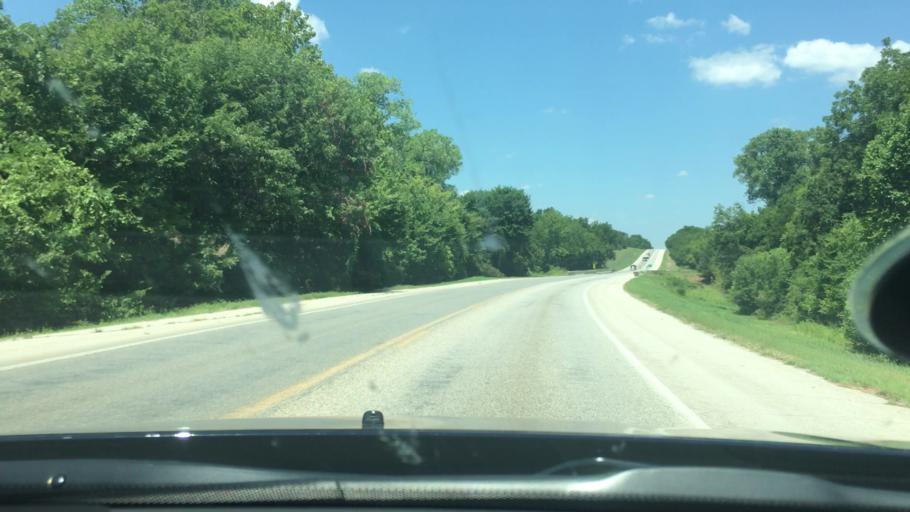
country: US
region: Oklahoma
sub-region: Marshall County
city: Oakland
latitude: 34.1745
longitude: -96.8562
